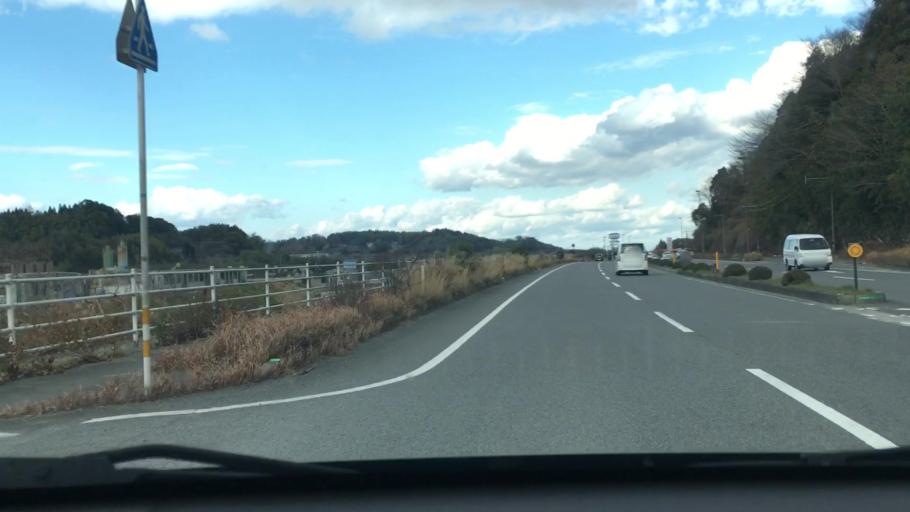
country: JP
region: Oita
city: Oita
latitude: 33.1202
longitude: 131.6537
